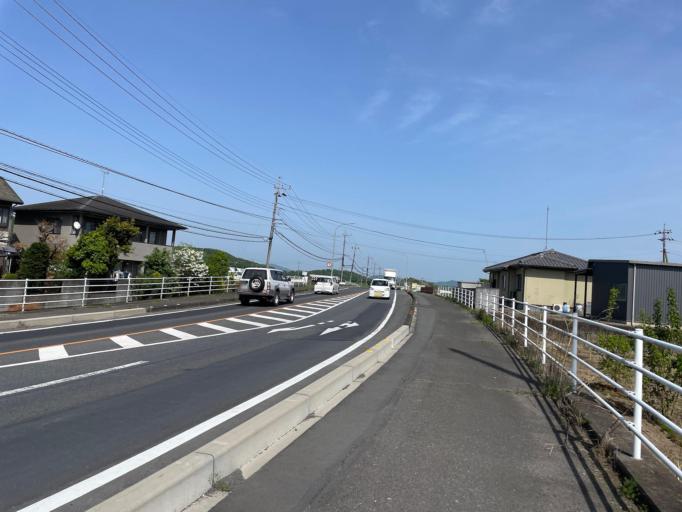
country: JP
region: Gunma
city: Tatebayashi
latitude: 36.3050
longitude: 139.5136
